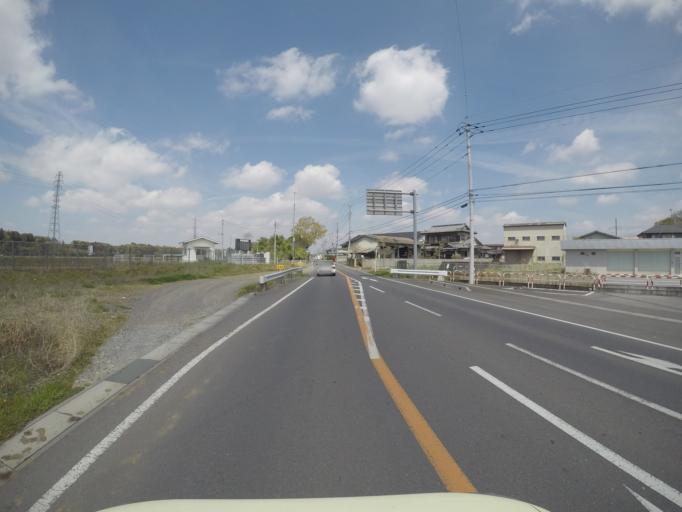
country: JP
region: Ibaraki
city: Shimodate
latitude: 36.2568
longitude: 140.0300
